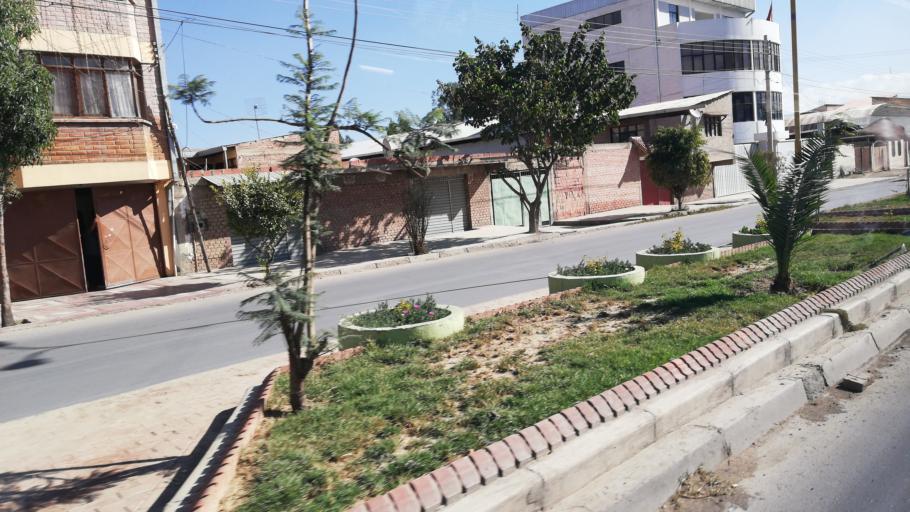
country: BO
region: Cochabamba
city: Cochabamba
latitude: -17.3935
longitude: -66.2472
